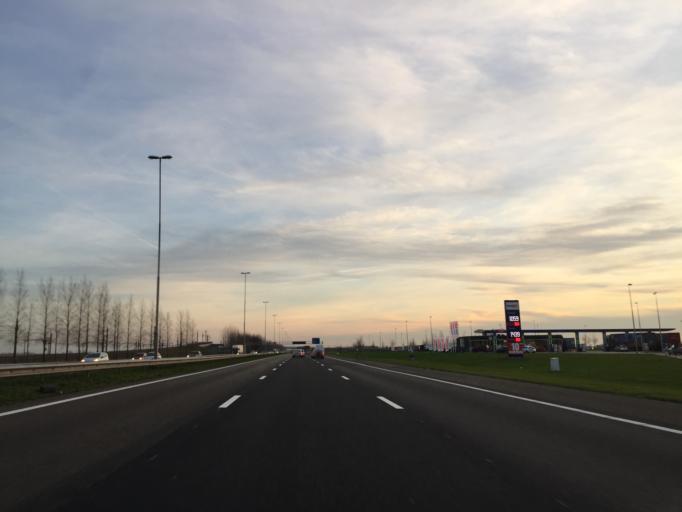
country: NL
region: North Brabant
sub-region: Gemeente Made en Drimmelen
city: Made
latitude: 51.6645
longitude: 4.6789
